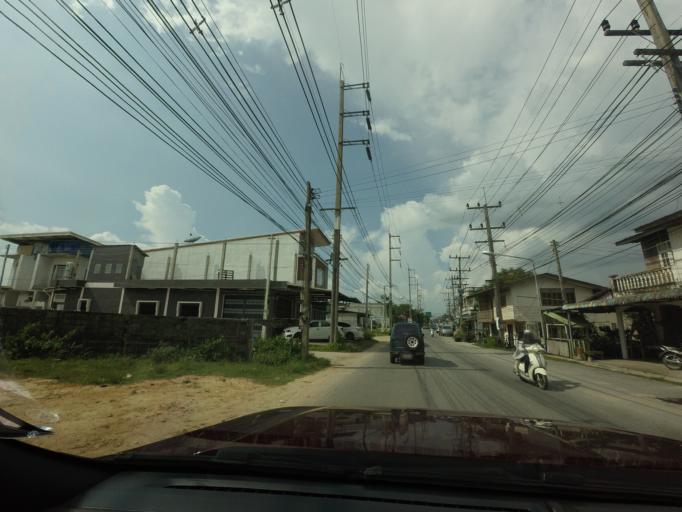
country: TH
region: Yala
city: Yala
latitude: 6.5119
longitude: 101.2710
